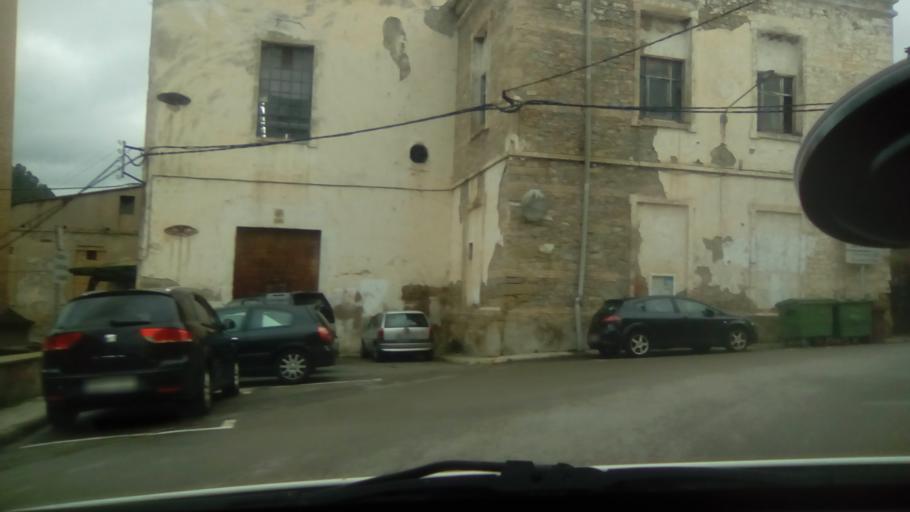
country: ES
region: Catalonia
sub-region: Provincia de Barcelona
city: Manresa
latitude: 41.6990
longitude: 1.8699
